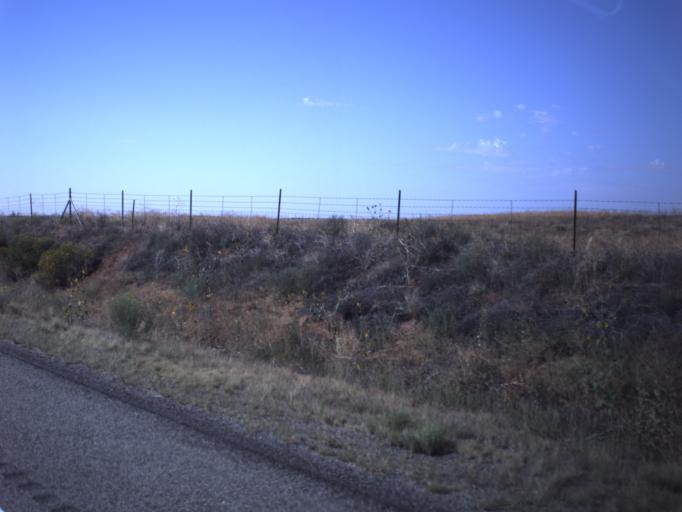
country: US
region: Utah
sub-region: San Juan County
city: Blanding
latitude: 37.4560
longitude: -109.4671
